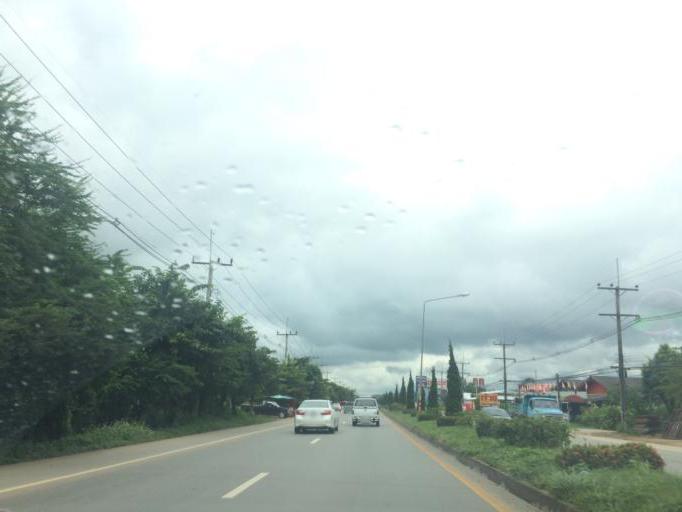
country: TH
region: Chiang Rai
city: Chiang Rai
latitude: 20.0177
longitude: 99.8700
